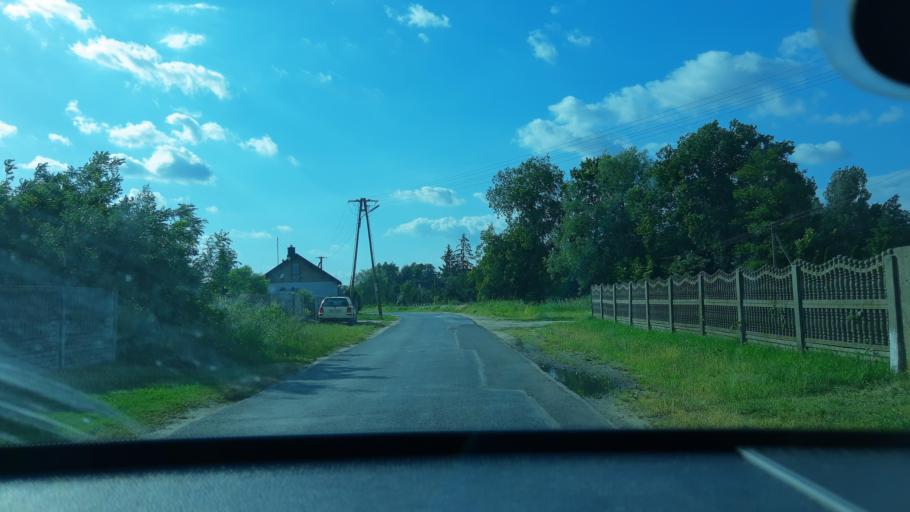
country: PL
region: Lodz Voivodeship
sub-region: Powiat zdunskowolski
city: Zapolice
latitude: 51.5250
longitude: 18.8425
